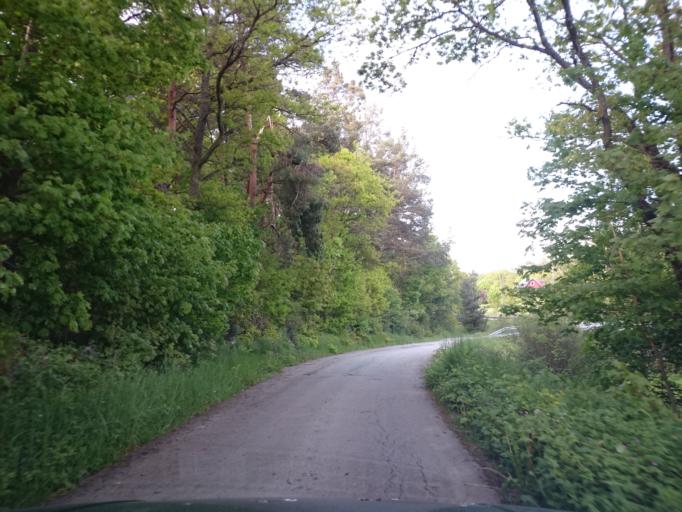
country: SE
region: Blekinge
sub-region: Karlshamns Kommun
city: Morrum
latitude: 56.1805
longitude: 14.7890
